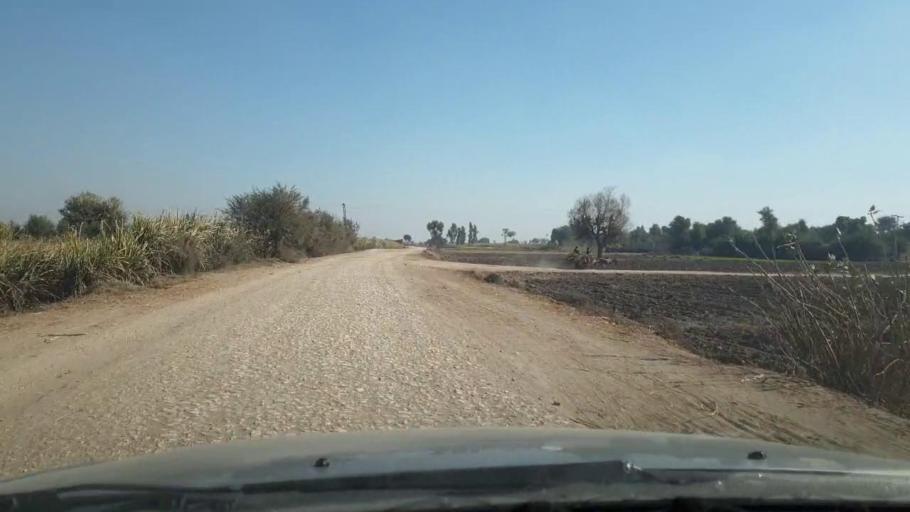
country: PK
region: Sindh
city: Ghotki
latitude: 28.0284
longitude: 69.2155
